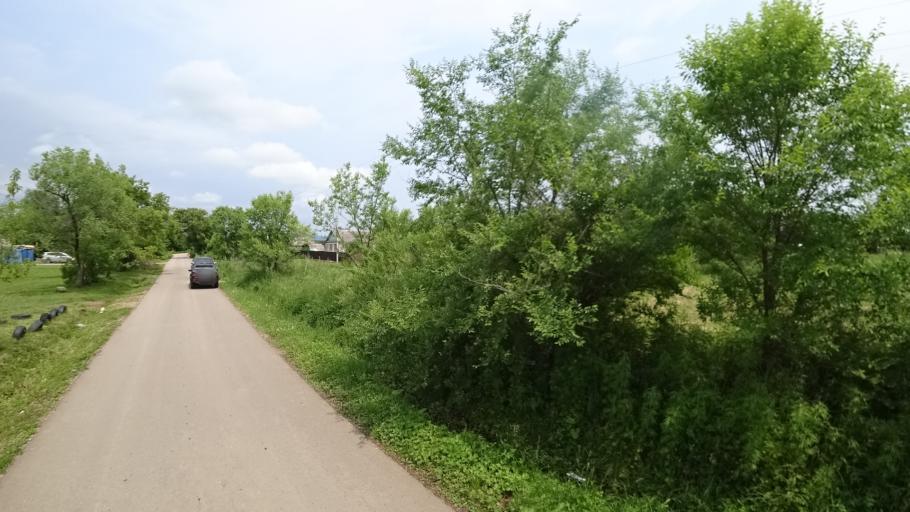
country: RU
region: Primorskiy
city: Novosysoyevka
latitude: 44.2376
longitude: 133.3584
